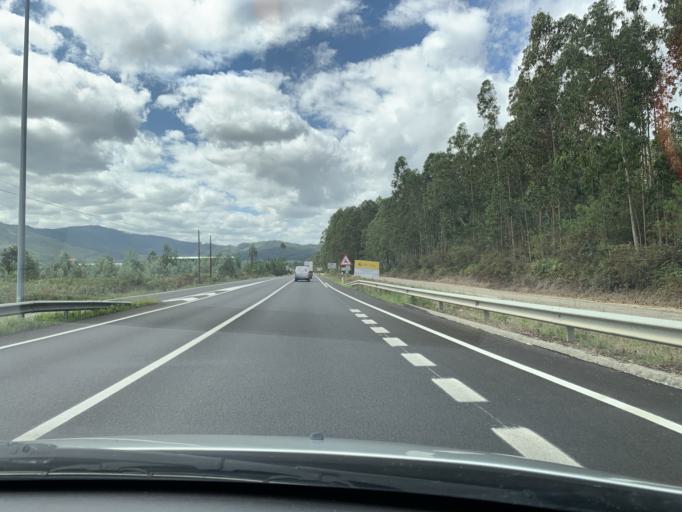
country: ES
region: Galicia
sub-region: Provincia de Lugo
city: Barreiros
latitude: 43.5404
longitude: -7.2542
